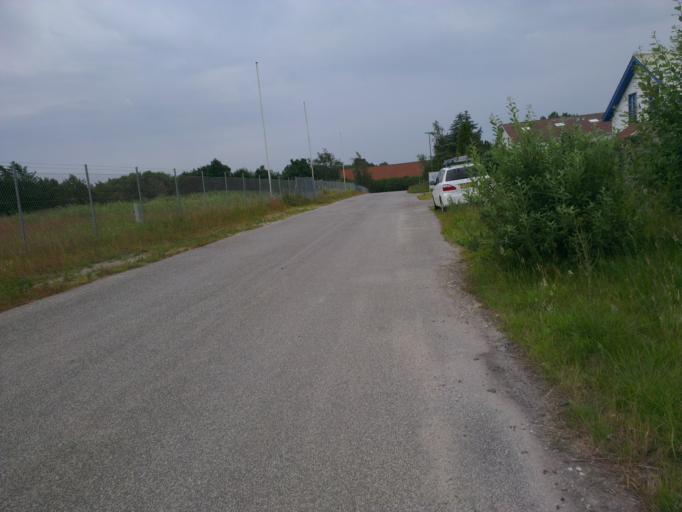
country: DK
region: Capital Region
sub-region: Frederikssund Kommune
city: Skibby
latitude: 55.7623
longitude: 11.9599
